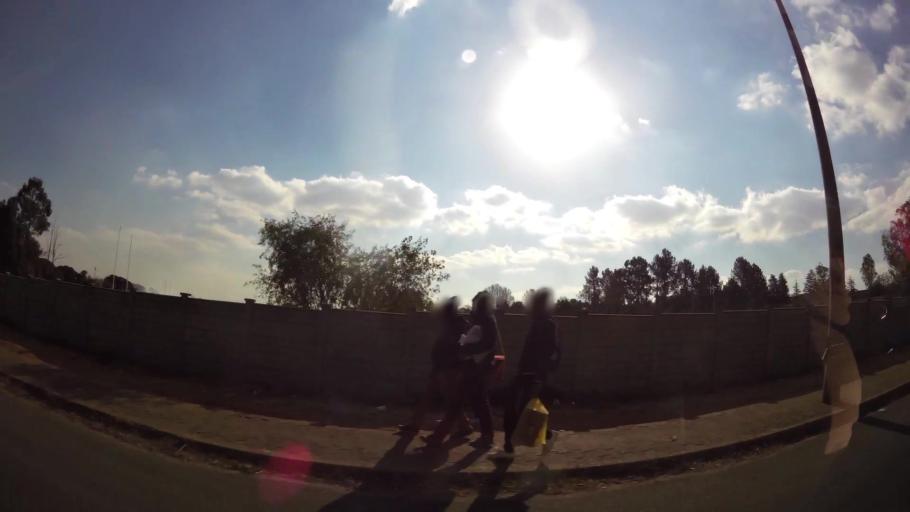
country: ZA
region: Gauteng
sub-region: West Rand District Municipality
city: Krugersdorp
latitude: -26.0961
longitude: 27.7757
